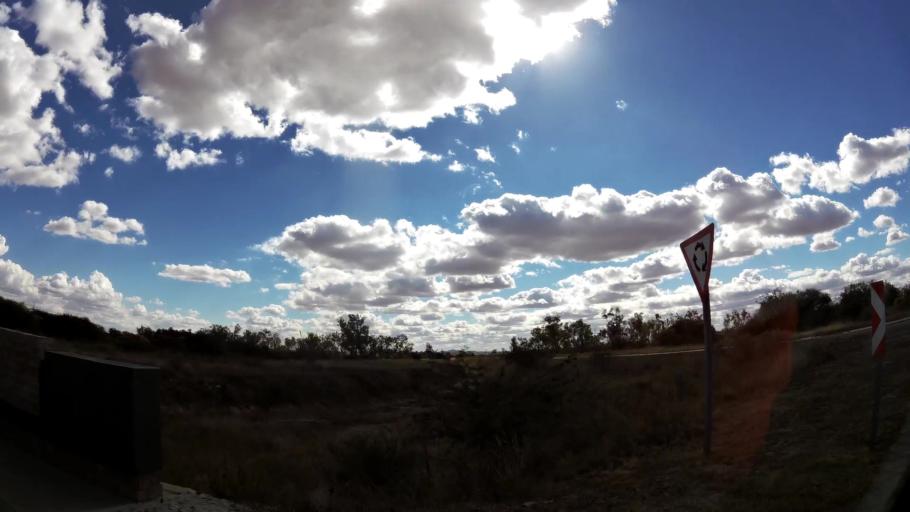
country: ZA
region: Limpopo
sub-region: Capricorn District Municipality
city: Polokwane
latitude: -23.8727
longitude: 29.4904
